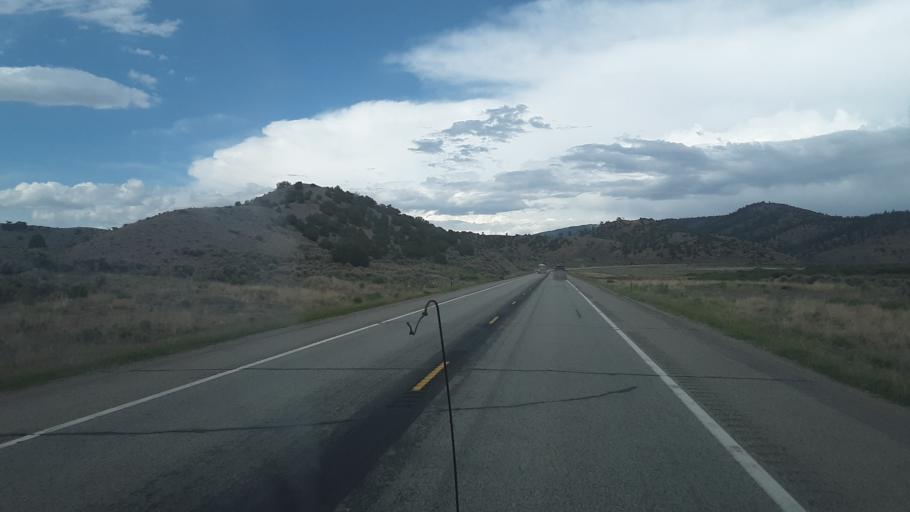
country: US
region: Colorado
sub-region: Costilla County
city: San Luis
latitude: 37.5098
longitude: -105.3166
